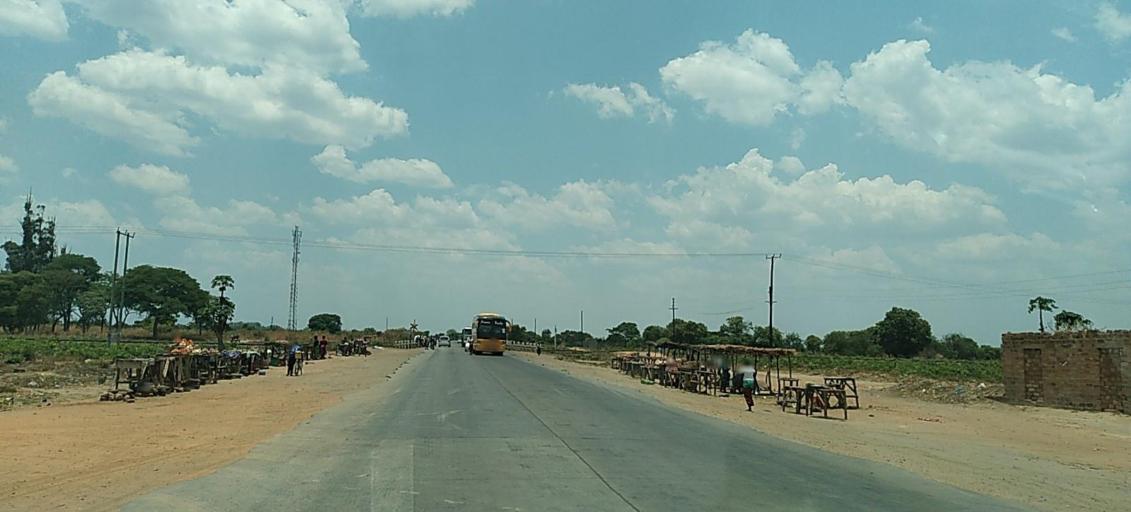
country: ZM
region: Central
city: Kapiri Mposhi
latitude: -13.8927
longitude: 28.6569
